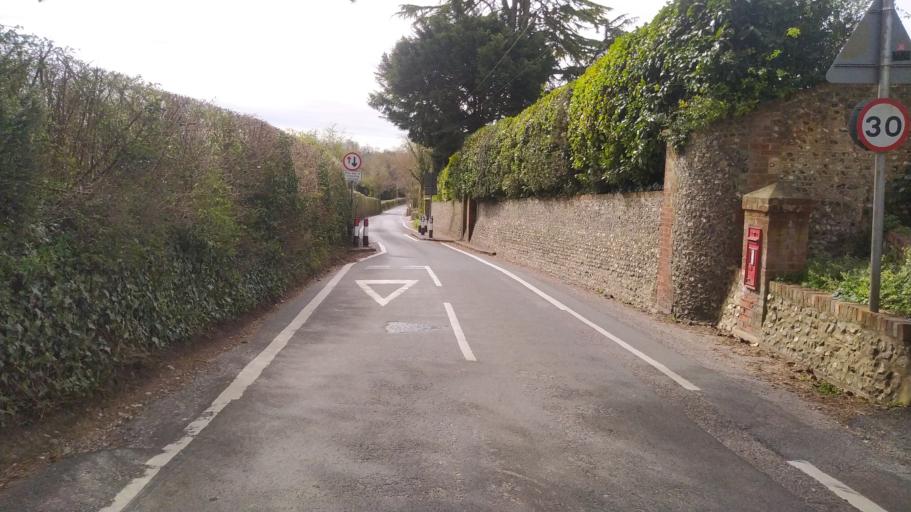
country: GB
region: England
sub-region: Hampshire
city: Bishops Waltham
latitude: 50.9656
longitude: -1.2086
